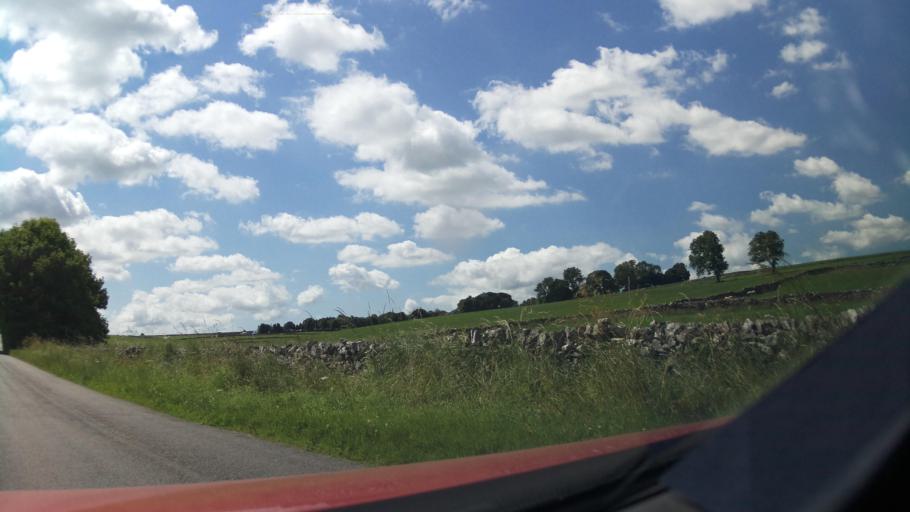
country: GB
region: England
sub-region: Derbyshire
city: Tideswell
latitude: 53.1867
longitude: -1.7794
